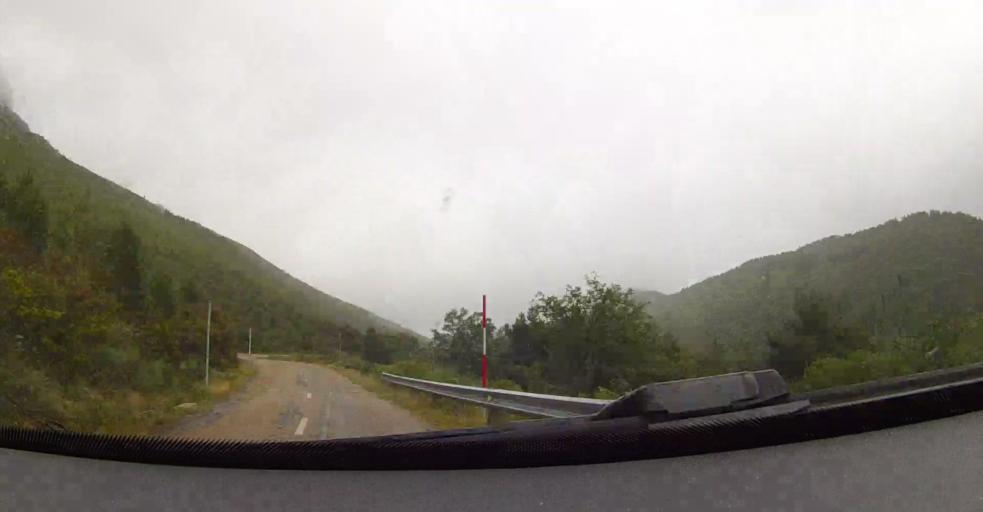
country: ES
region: Castille and Leon
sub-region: Provincia de Leon
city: Puebla de Lillo
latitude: 43.0740
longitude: -5.2633
